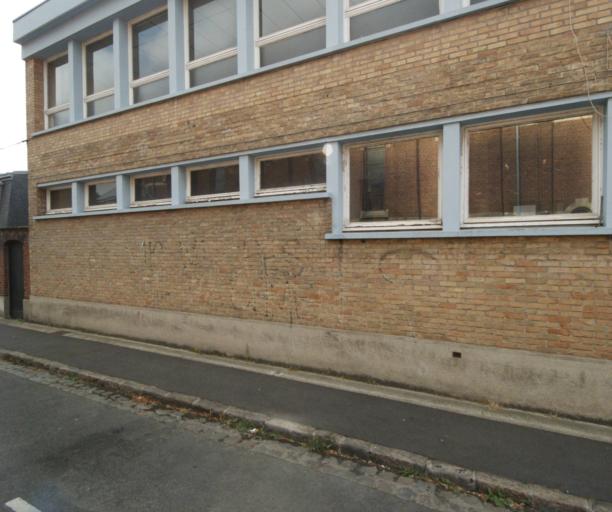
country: FR
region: Nord-Pas-de-Calais
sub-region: Departement du Nord
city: Armentieres
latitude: 50.6868
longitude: 2.8758
